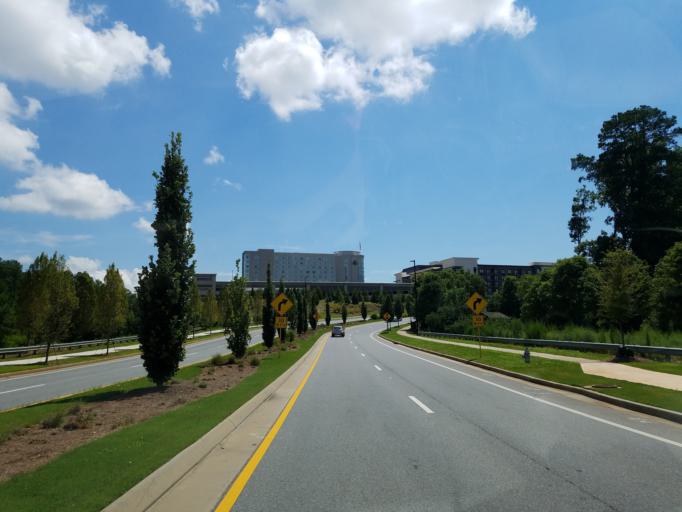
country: US
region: Georgia
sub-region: Fulton County
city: Alpharetta
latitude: 34.0740
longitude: -84.2718
